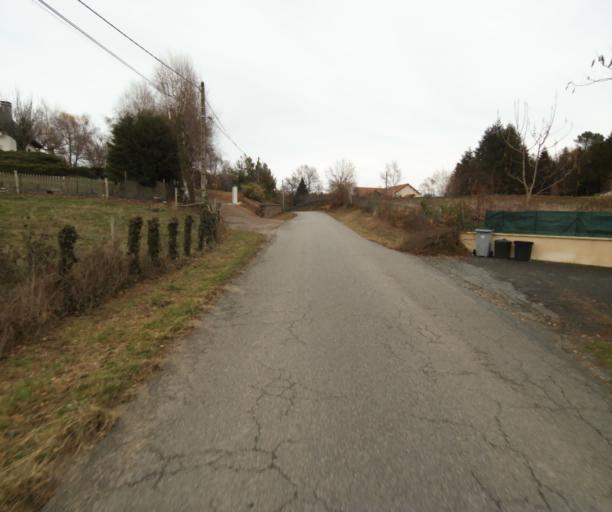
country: FR
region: Limousin
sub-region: Departement de la Correze
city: Saint-Mexant
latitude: 45.2616
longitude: 1.6640
